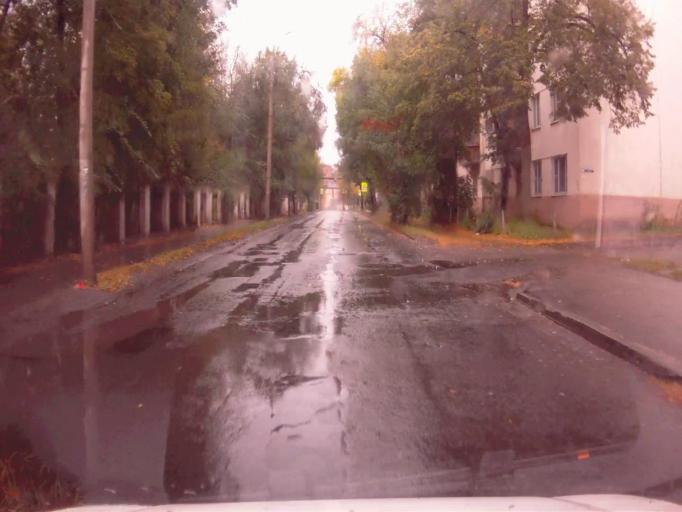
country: RU
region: Chelyabinsk
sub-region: Gorod Chelyabinsk
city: Chelyabinsk
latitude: 55.1925
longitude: 61.4118
